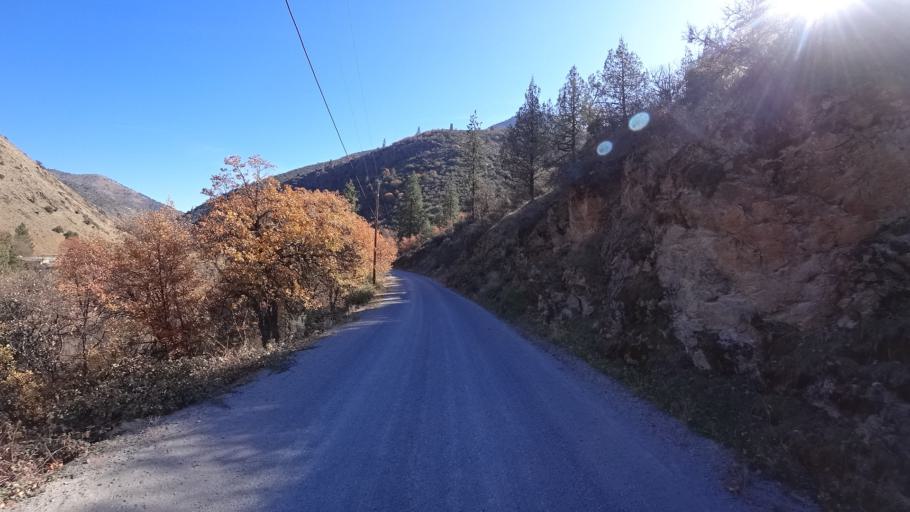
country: US
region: California
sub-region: Siskiyou County
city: Yreka
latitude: 41.8316
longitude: -122.6329
